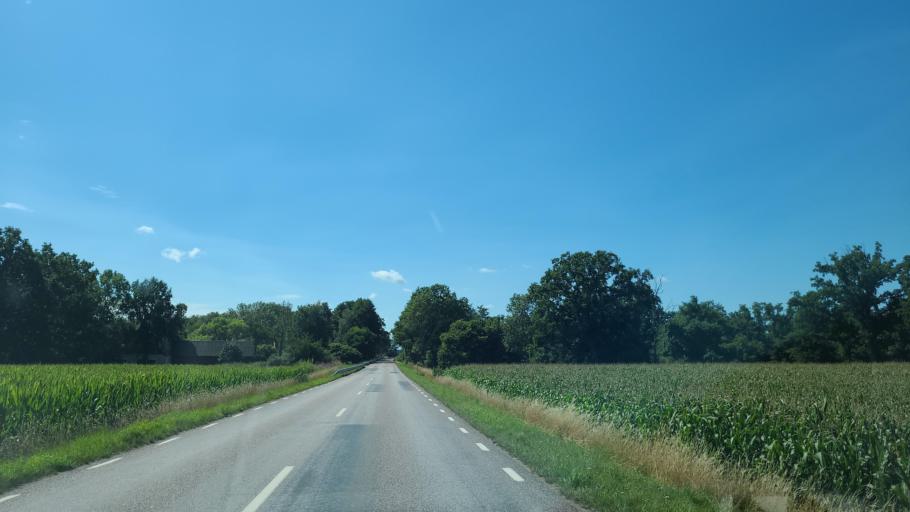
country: SE
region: Kalmar
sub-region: Kalmar Kommun
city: Ljungbyholm
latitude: 56.5844
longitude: 16.1129
